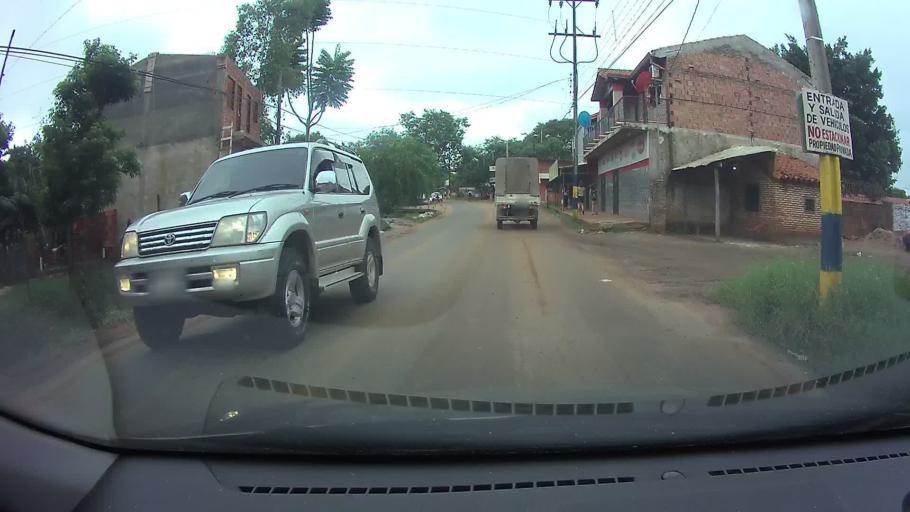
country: PY
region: Central
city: San Lorenzo
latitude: -25.3137
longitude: -57.4930
